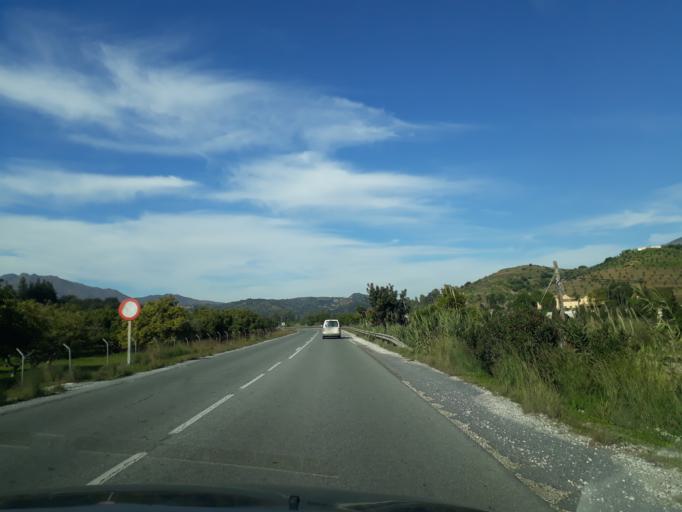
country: ES
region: Andalusia
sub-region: Provincia de Malaga
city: Fuengirola
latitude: 36.5452
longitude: -4.6884
